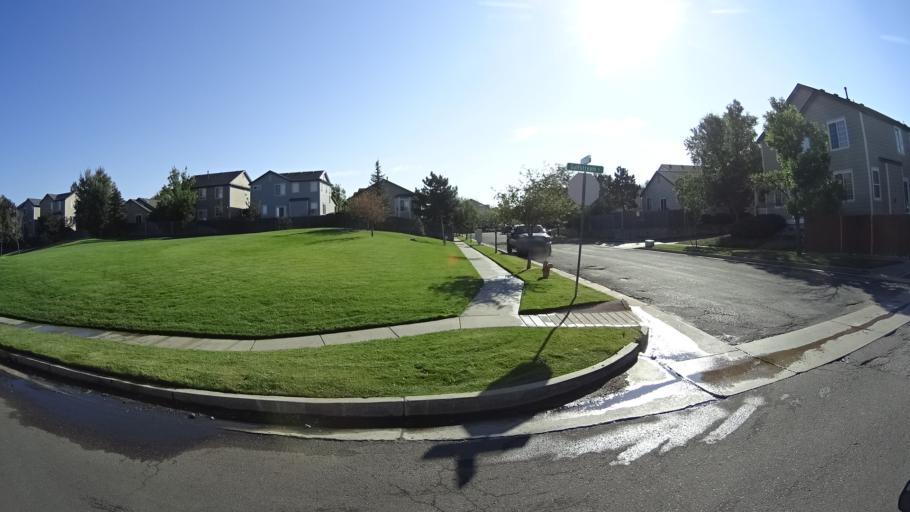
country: US
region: Colorado
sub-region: El Paso County
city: Cimarron Hills
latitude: 38.8773
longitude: -104.6972
